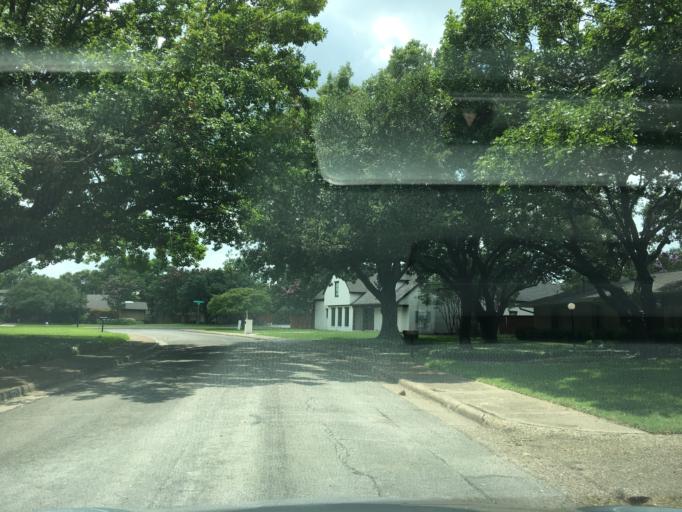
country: US
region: Texas
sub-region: Dallas County
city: University Park
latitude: 32.8919
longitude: -96.7851
